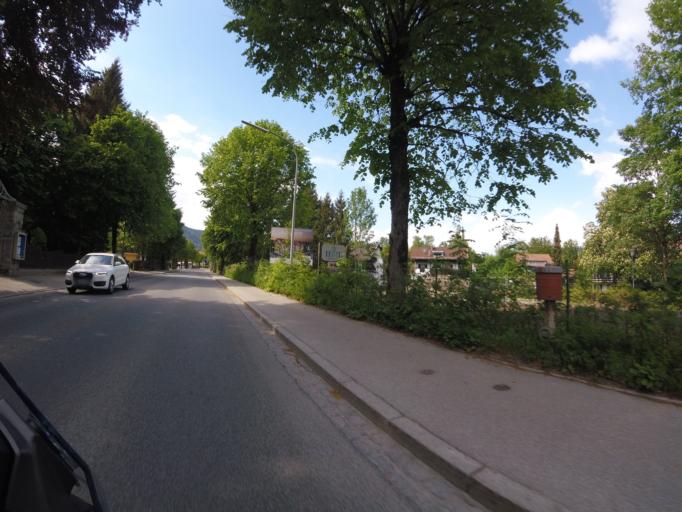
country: DE
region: Bavaria
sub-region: Upper Bavaria
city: Bad Wiessee
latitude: 47.7157
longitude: 11.7211
